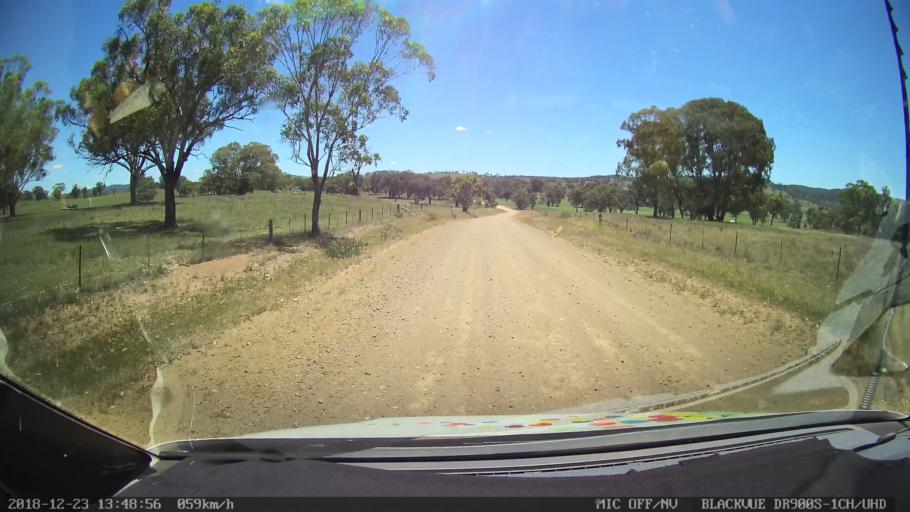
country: AU
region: New South Wales
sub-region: Tamworth Municipality
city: Manilla
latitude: -30.5198
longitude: 151.1126
